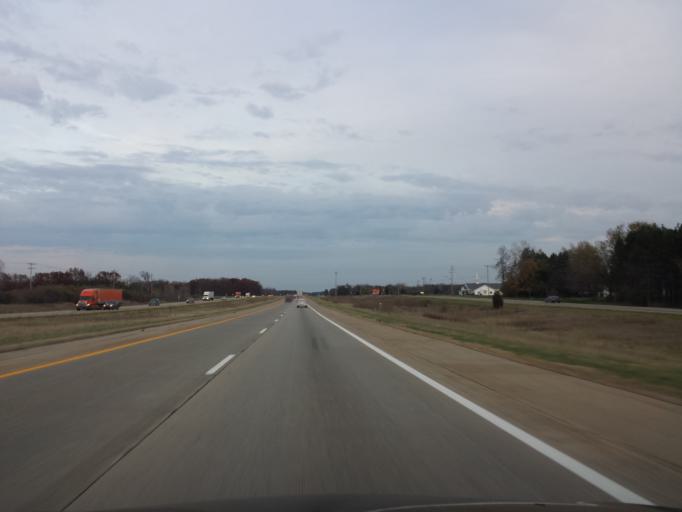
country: US
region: Michigan
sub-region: Shiawassee County
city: Laingsburg
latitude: 42.8078
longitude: -84.3165
